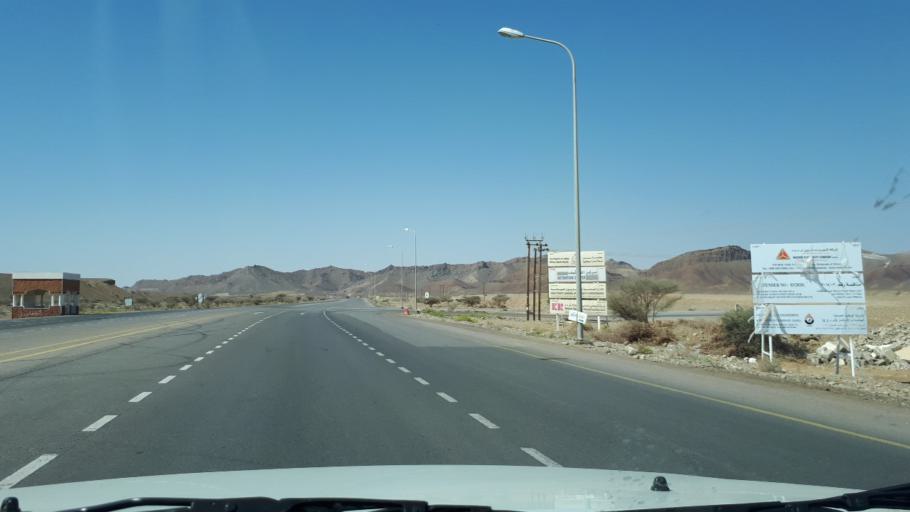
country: OM
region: Ash Sharqiyah
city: Sur
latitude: 22.3735
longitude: 59.3187
